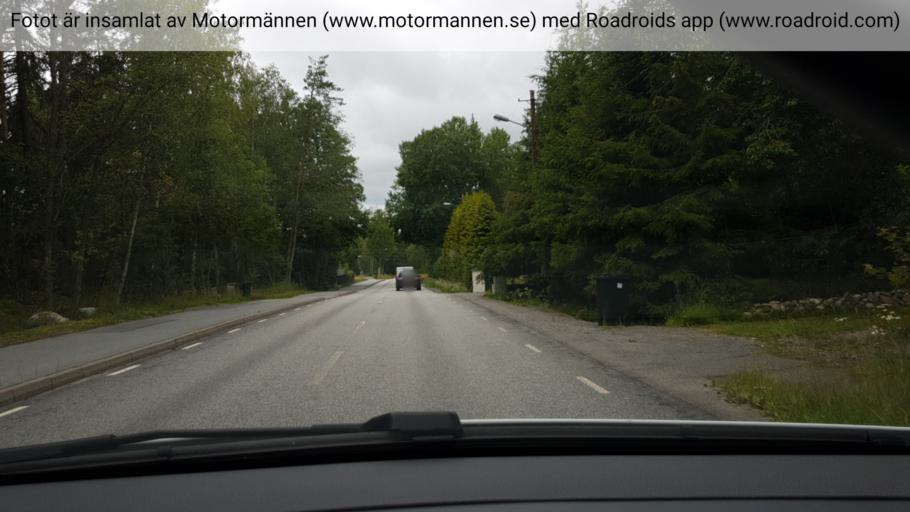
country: SE
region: Stockholm
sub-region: Vaxholms Kommun
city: Vaxholm
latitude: 59.4015
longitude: 18.3811
